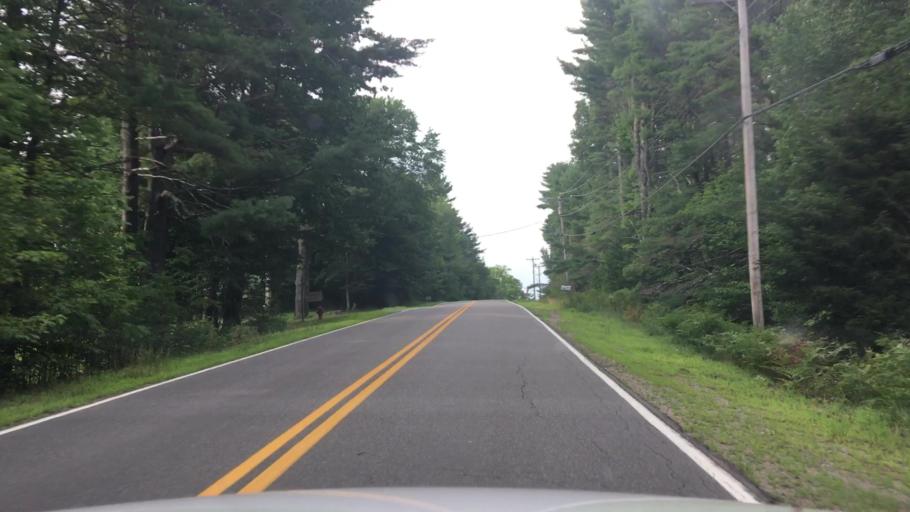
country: US
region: Maine
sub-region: Knox County
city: Washington
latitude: 44.2627
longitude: -69.3736
